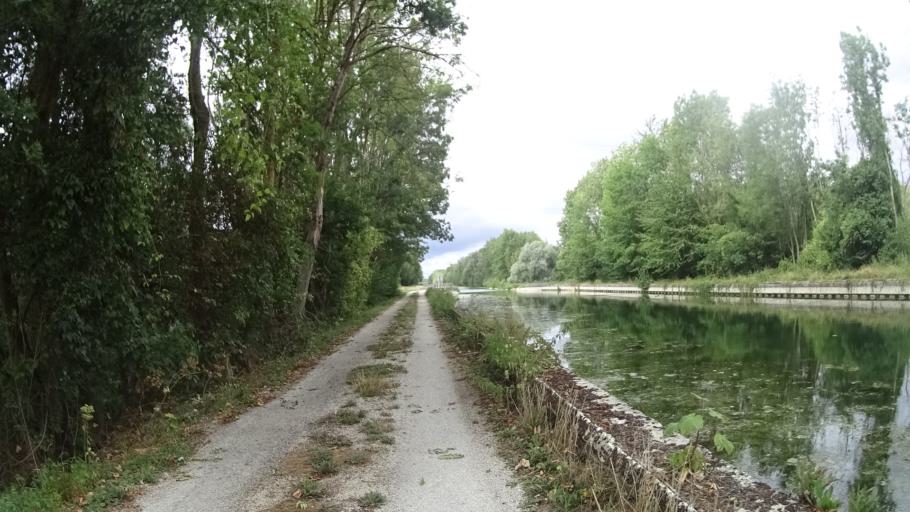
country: FR
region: Picardie
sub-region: Departement de l'Aisne
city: La Fere
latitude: 49.7025
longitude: 3.3695
